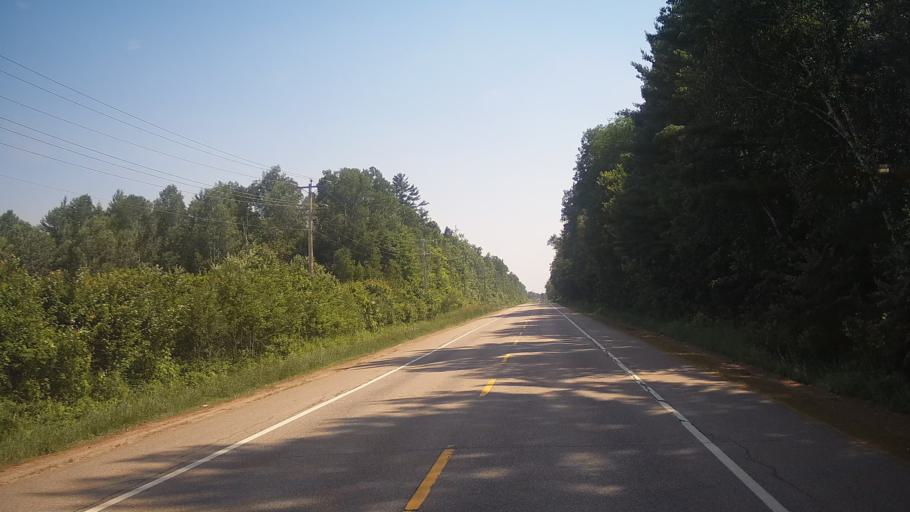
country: CA
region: Ontario
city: Pembroke
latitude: 45.8426
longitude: -77.0135
